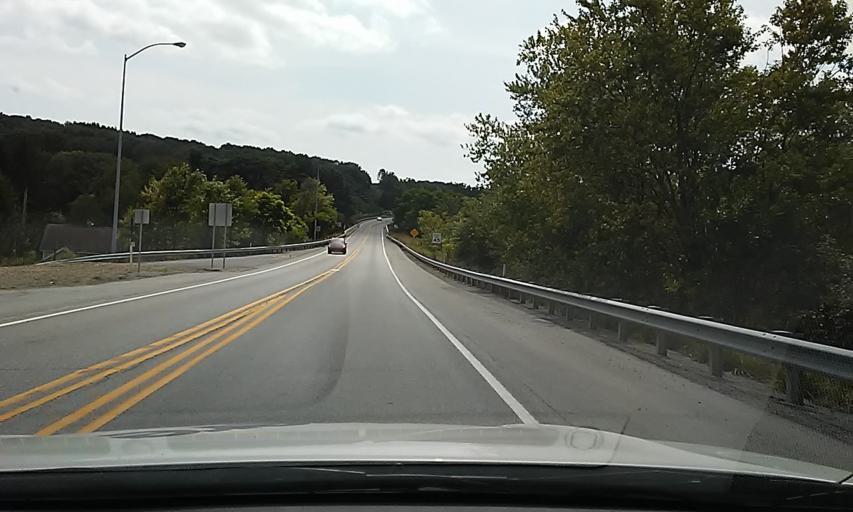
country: US
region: Pennsylvania
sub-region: Jefferson County
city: Punxsutawney
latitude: 40.9385
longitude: -78.9758
